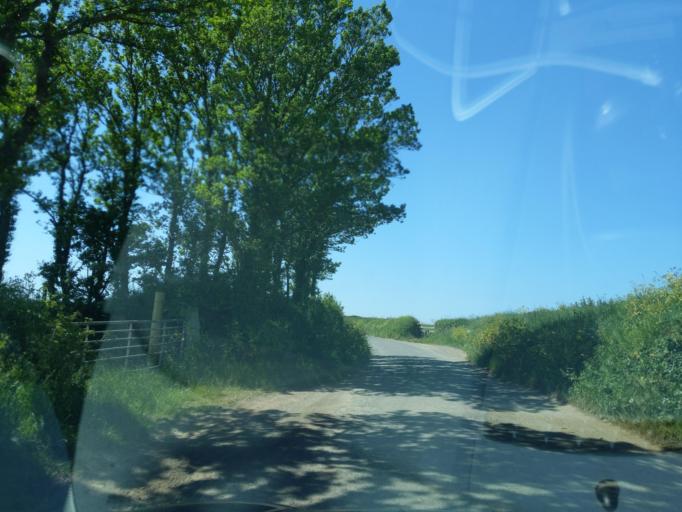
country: GB
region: England
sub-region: Cornwall
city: Wadebridge
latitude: 50.5802
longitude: -4.8332
